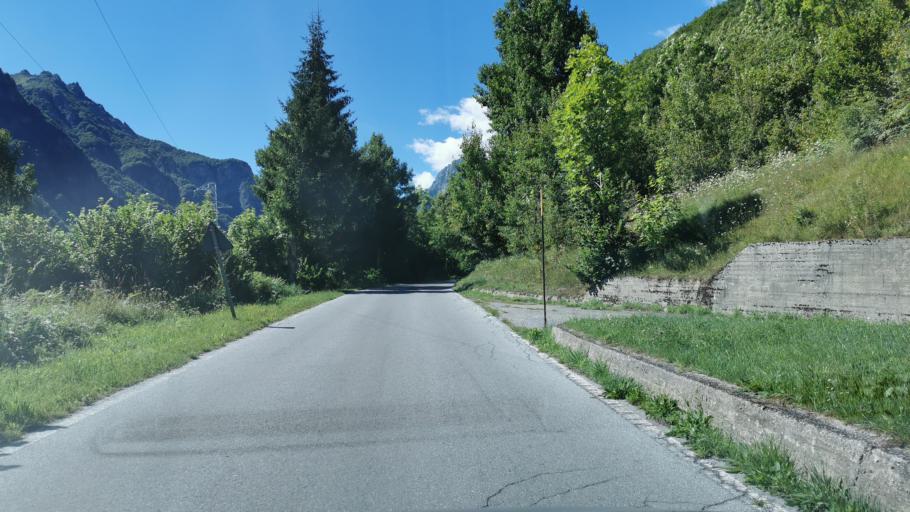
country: IT
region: Piedmont
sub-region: Provincia di Cuneo
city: Entracque
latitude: 44.2302
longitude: 7.3893
